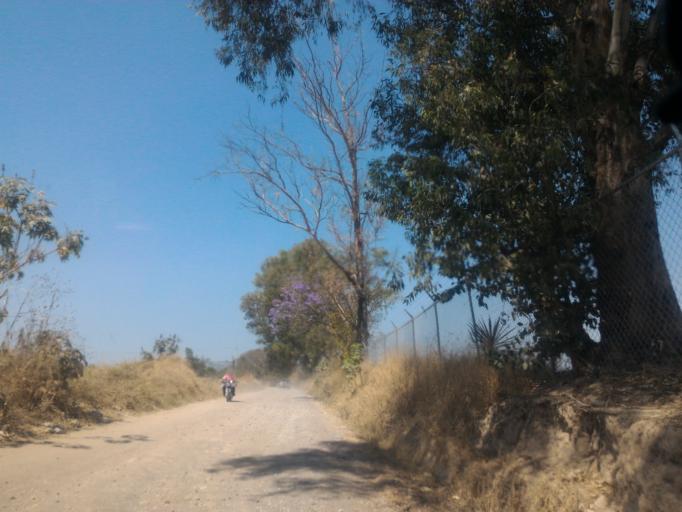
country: MX
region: Jalisco
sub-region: San Pedro Tlaquepaque
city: Paseo del Prado
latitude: 20.5635
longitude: -103.4045
